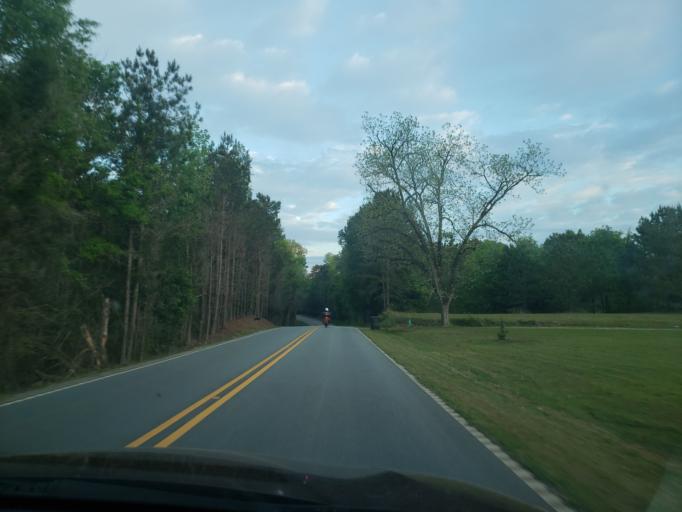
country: US
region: Alabama
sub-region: Tallapoosa County
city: Dadeville
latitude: 32.7067
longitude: -85.7633
